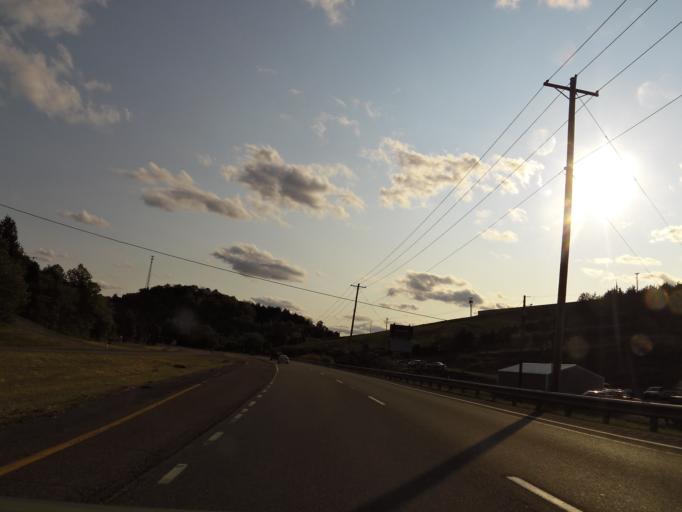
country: US
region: Virginia
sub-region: Tazewell County
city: Claypool Hill
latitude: 37.0407
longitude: -81.7934
